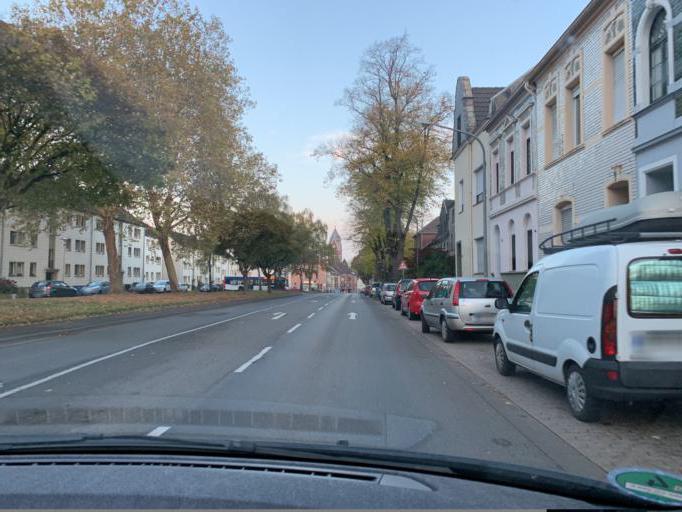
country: DE
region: North Rhine-Westphalia
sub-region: Regierungsbezirk Dusseldorf
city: Juchen
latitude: 51.1290
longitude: 6.4524
